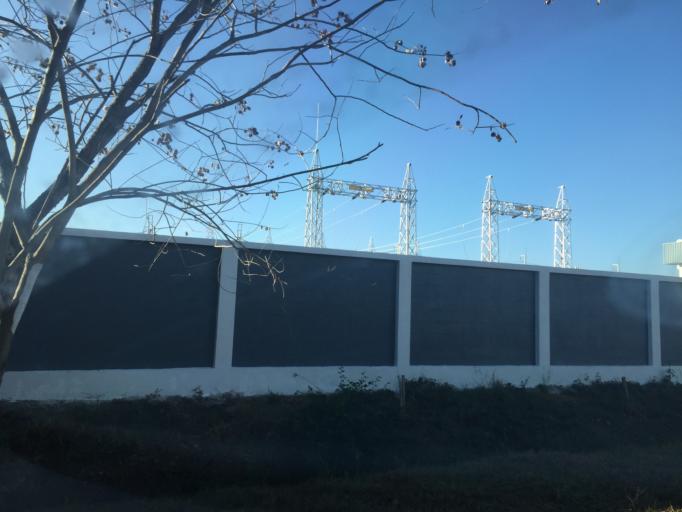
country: TH
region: Lamphun
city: Lamphun
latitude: 18.5955
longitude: 99.0504
